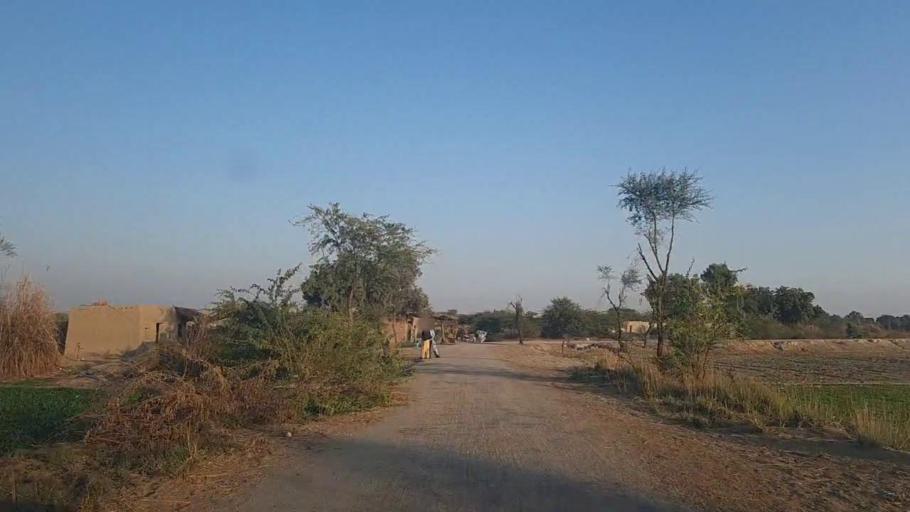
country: PK
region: Sindh
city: Jam Sahib
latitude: 26.3242
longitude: 68.6982
